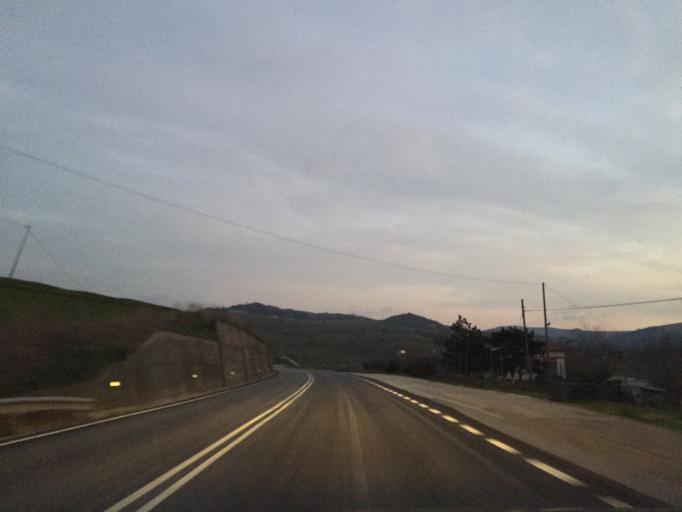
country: IT
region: Apulia
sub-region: Provincia di Foggia
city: Volturara Appula
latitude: 41.4626
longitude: 15.0585
